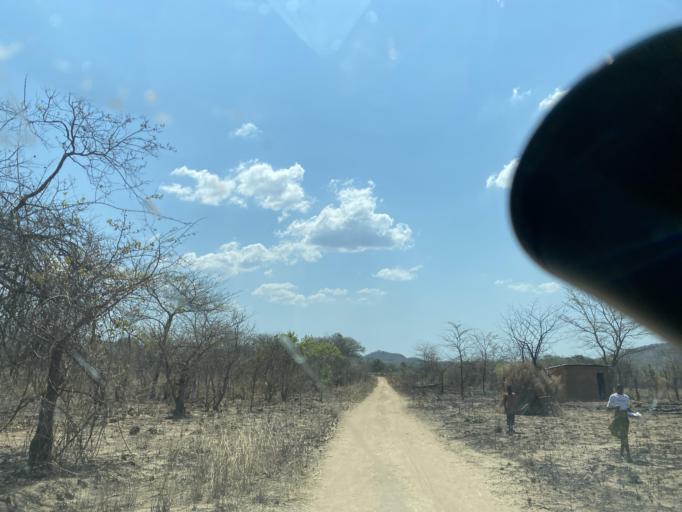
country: ZM
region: Lusaka
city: Chongwe
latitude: -15.0821
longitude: 29.5044
